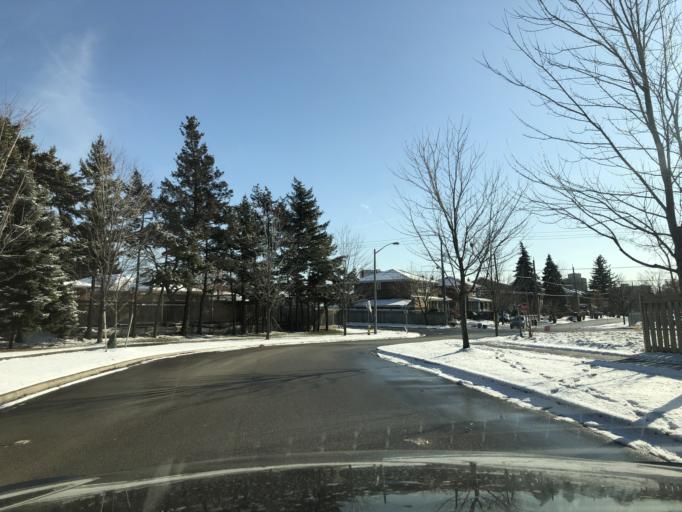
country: CA
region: Ontario
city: Etobicoke
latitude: 43.7096
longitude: -79.5281
